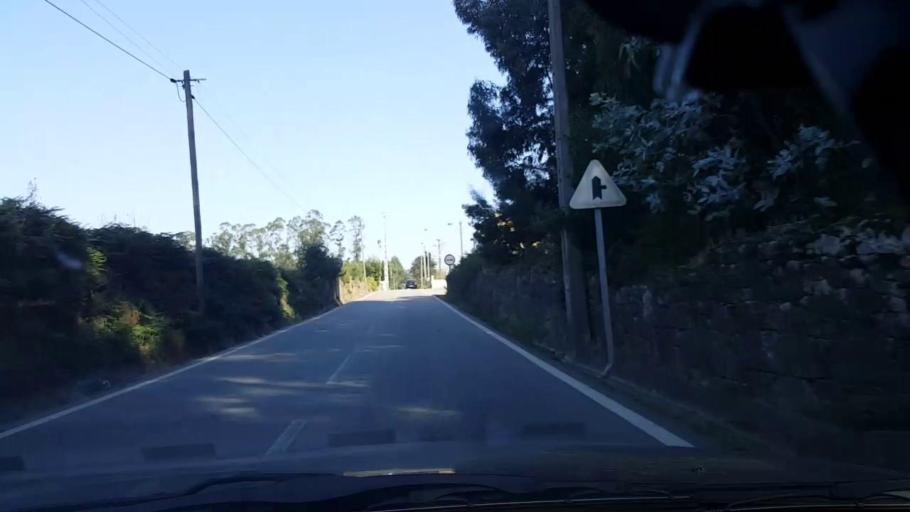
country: PT
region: Porto
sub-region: Vila do Conde
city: Arvore
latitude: 41.3175
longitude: -8.6793
